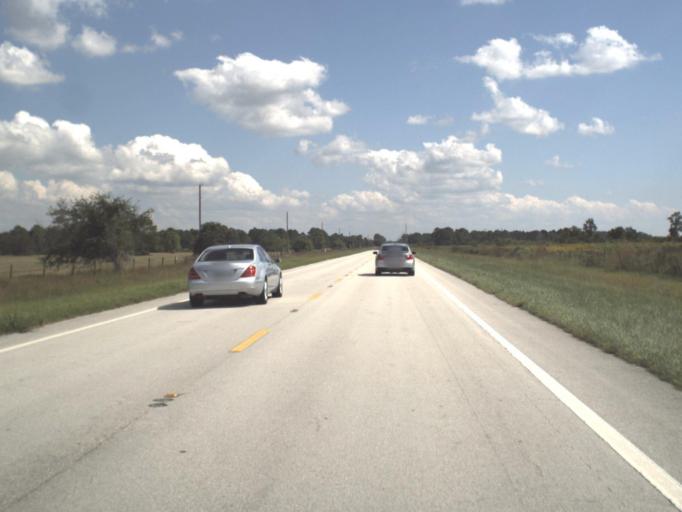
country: US
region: Florida
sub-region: Okeechobee County
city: Okeechobee
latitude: 27.3698
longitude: -81.0776
